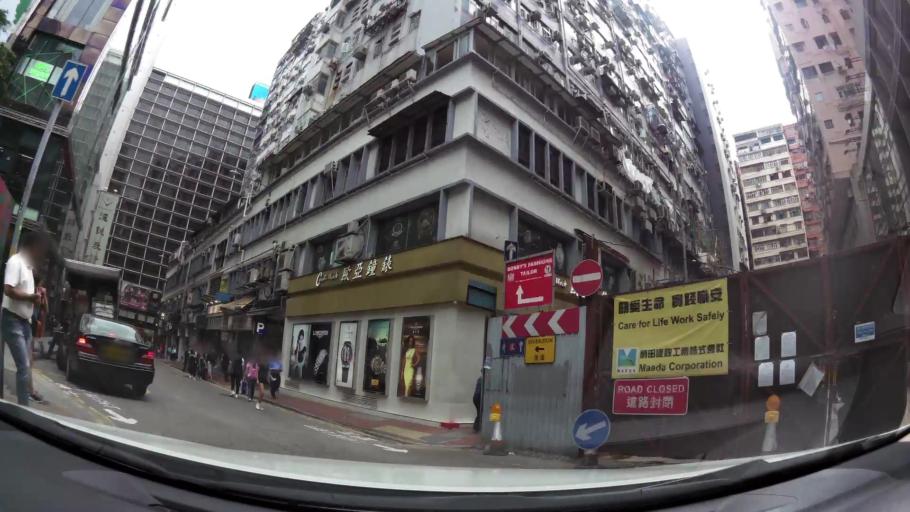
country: HK
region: Wanchai
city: Wan Chai
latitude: 22.2977
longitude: 114.1732
